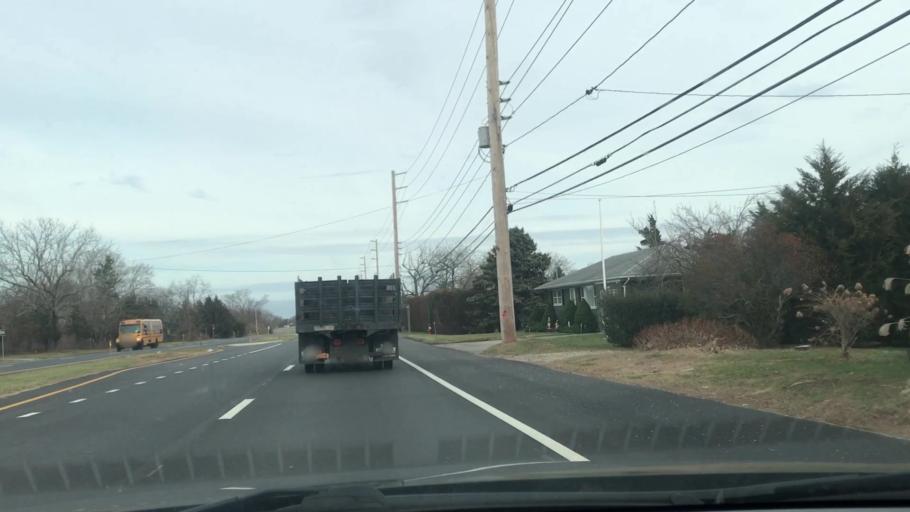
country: US
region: New York
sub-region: Suffolk County
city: Southold
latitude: 41.0501
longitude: -72.4598
